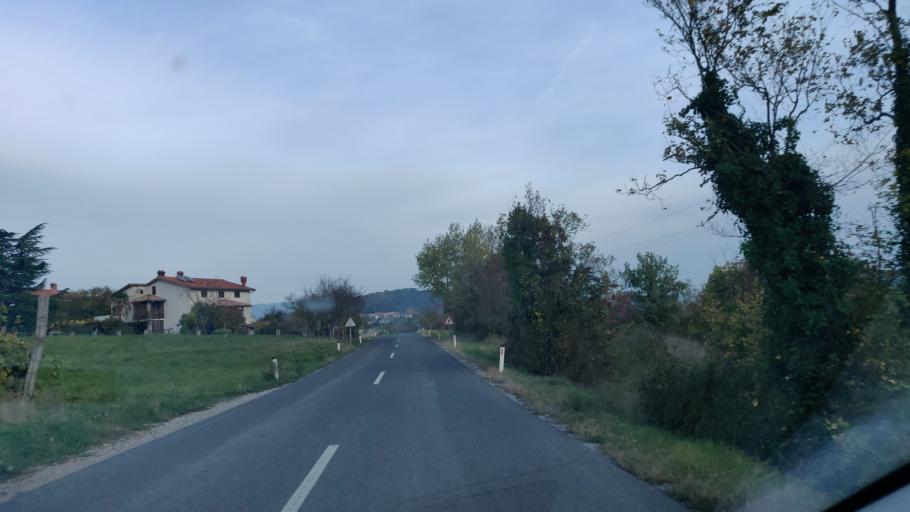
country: SI
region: Komen
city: Komen
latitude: 45.8196
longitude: 13.8391
